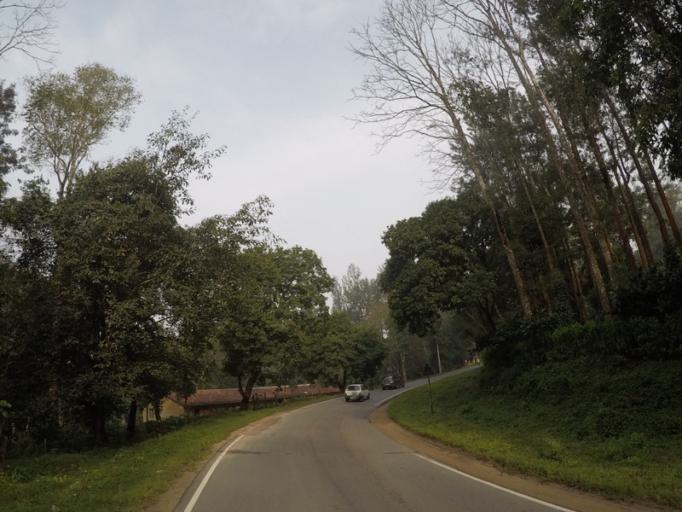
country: IN
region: Karnataka
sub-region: Chikmagalur
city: Mudigere
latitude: 13.2604
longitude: 75.6307
